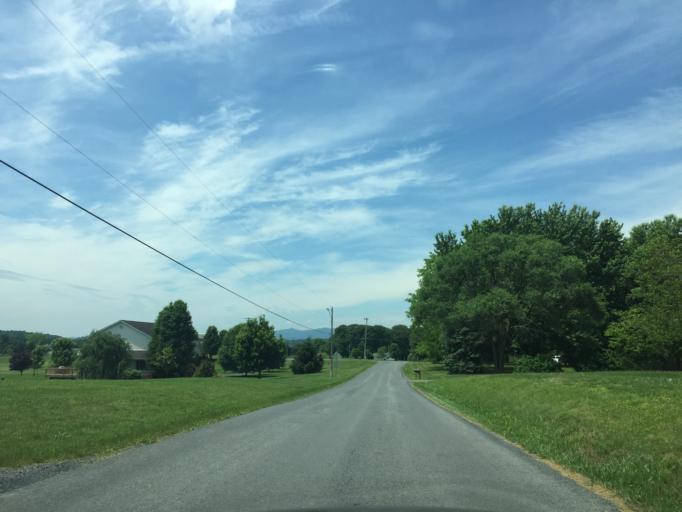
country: US
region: Virginia
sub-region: Warren County
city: Front Royal
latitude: 38.9800
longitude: -78.1623
